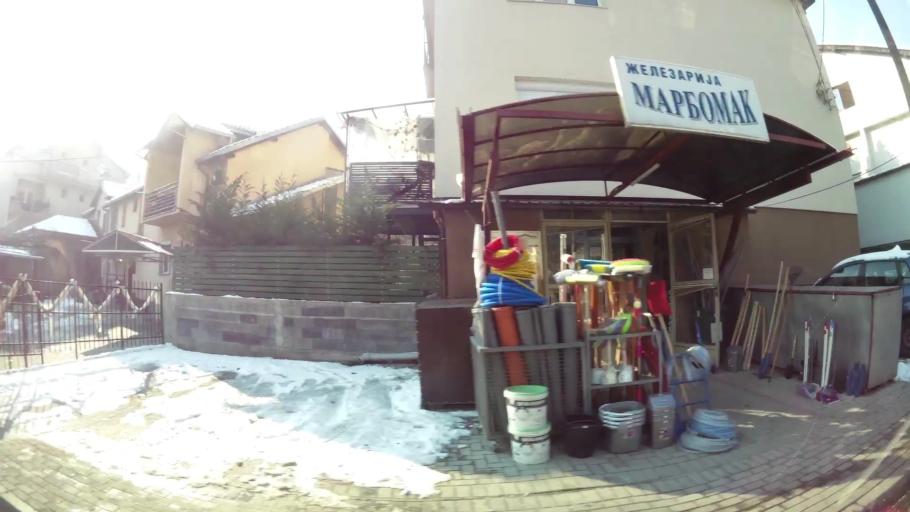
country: MK
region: Karpos
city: Skopje
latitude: 41.9833
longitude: 21.4306
